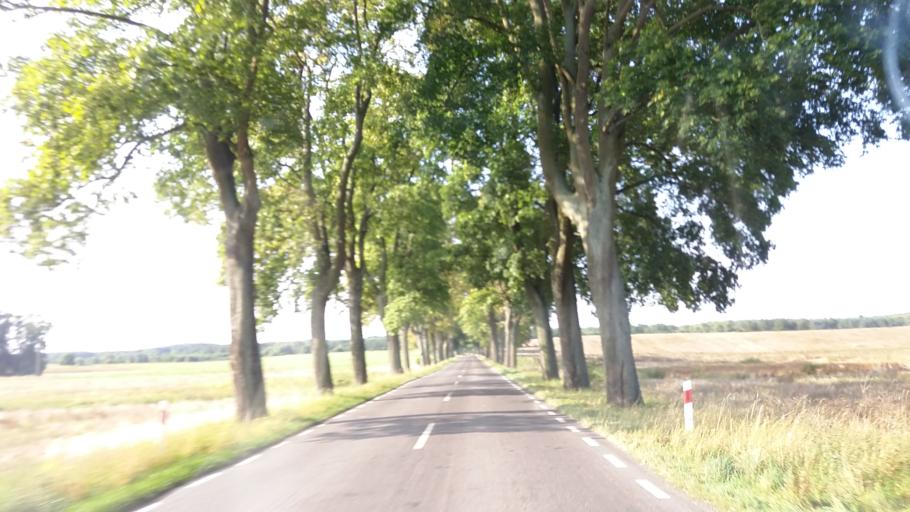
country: PL
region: West Pomeranian Voivodeship
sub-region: Powiat choszczenski
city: Choszczno
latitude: 53.2216
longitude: 15.4771
